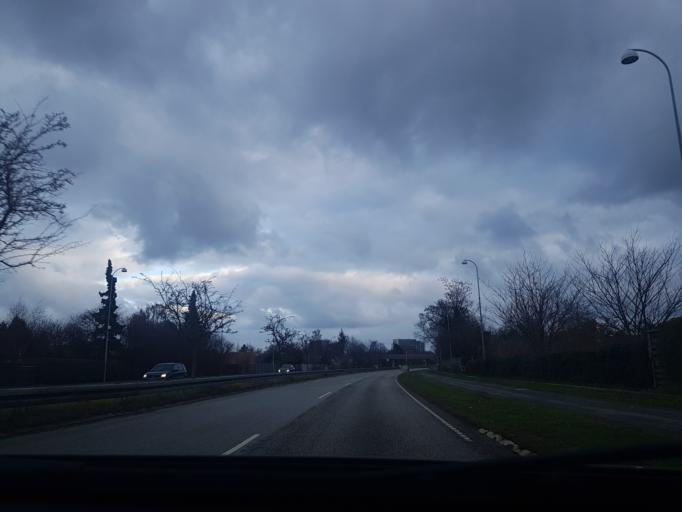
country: DK
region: Capital Region
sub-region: Vallensbaek Kommune
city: Vallensbaek
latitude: 55.6210
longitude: 12.3813
